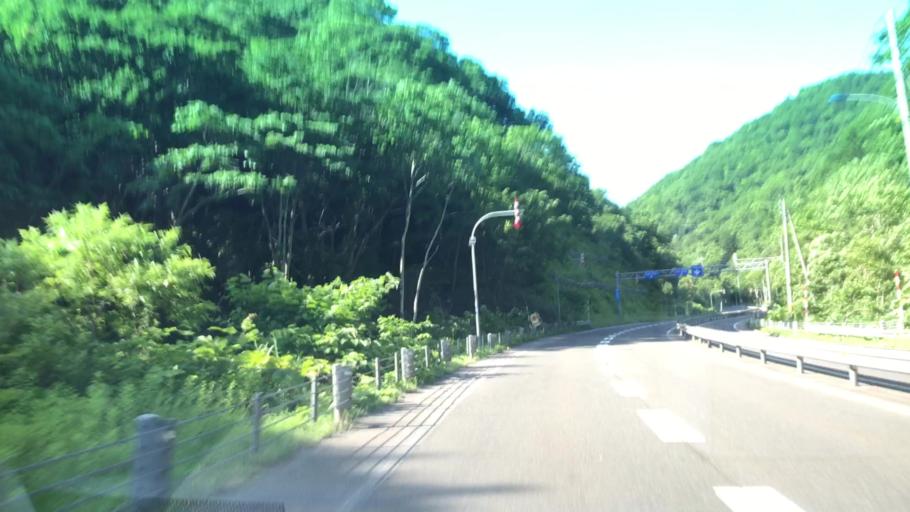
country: JP
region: Hokkaido
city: Iwanai
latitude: 43.0410
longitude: 140.6797
